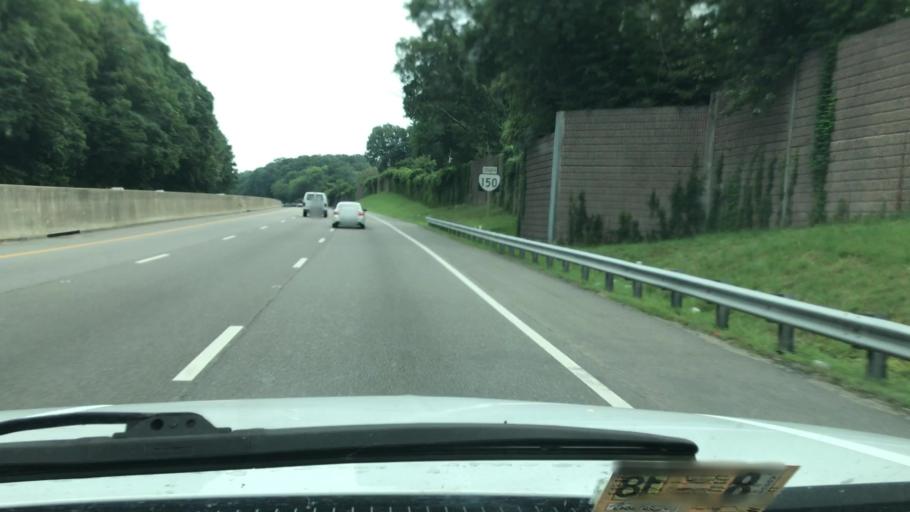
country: US
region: Virginia
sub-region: Chesterfield County
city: Bon Air
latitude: 37.4734
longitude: -77.5129
